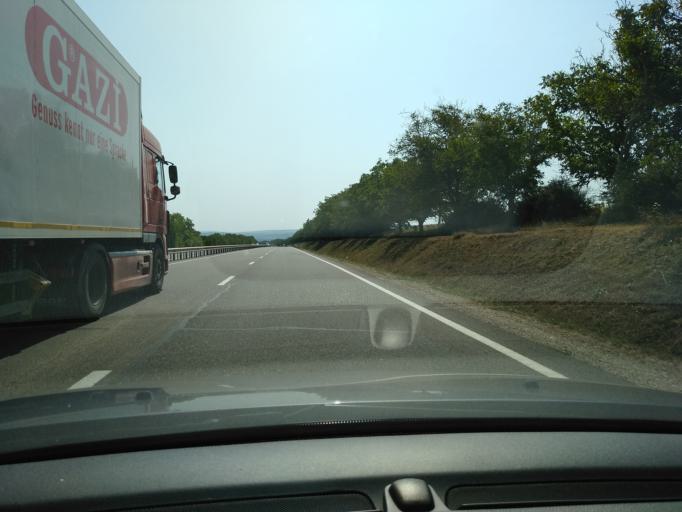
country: MD
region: Chisinau
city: Cricova
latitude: 47.2114
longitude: 28.7700
